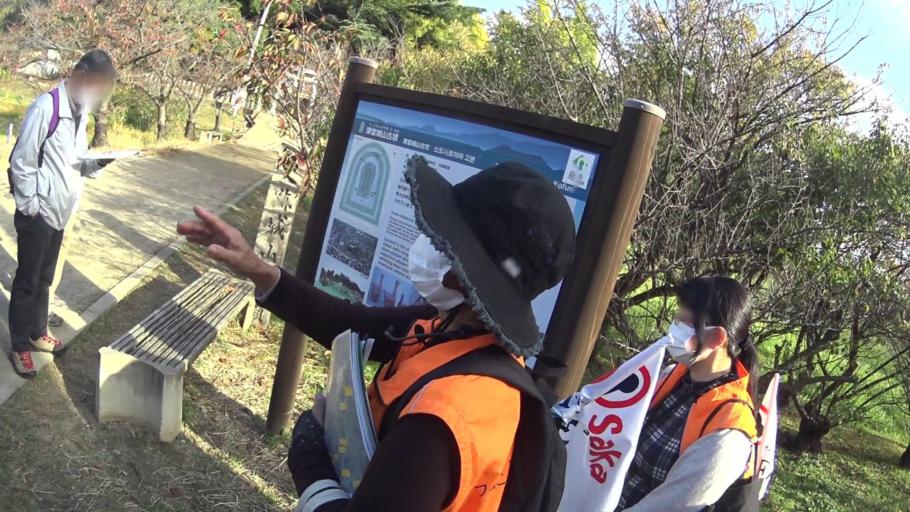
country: JP
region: Osaka
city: Kashihara
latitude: 34.5820
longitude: 135.5925
